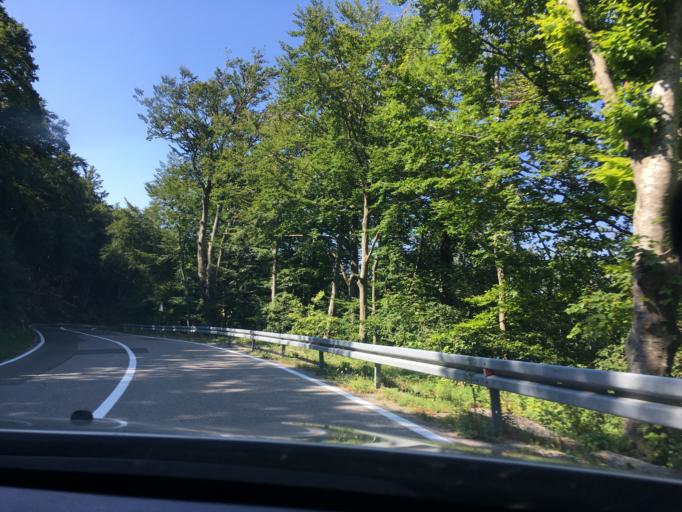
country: HR
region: Primorsko-Goranska
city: Hreljin
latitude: 45.3506
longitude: 14.6175
